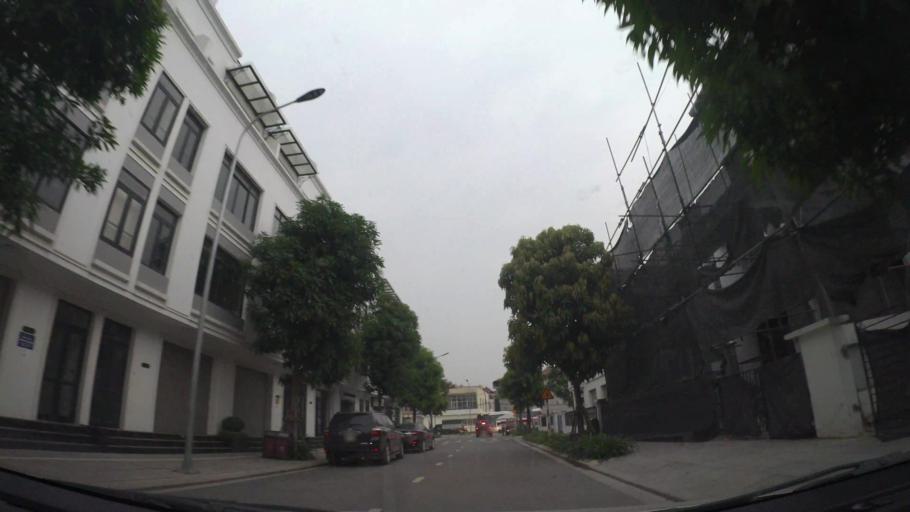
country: VN
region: Ha Noi
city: Cau Dien
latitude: 21.0373
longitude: 105.7606
